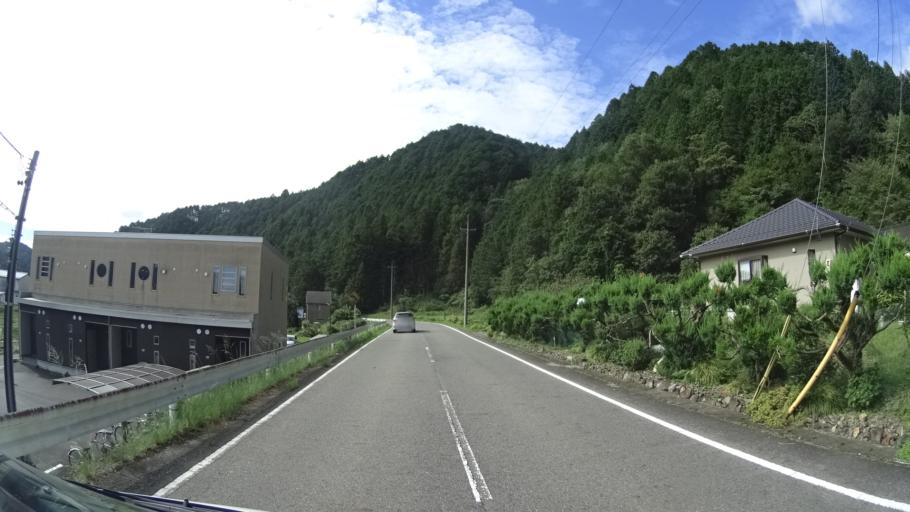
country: JP
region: Gifu
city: Minokamo
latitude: 35.5845
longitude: 137.0841
